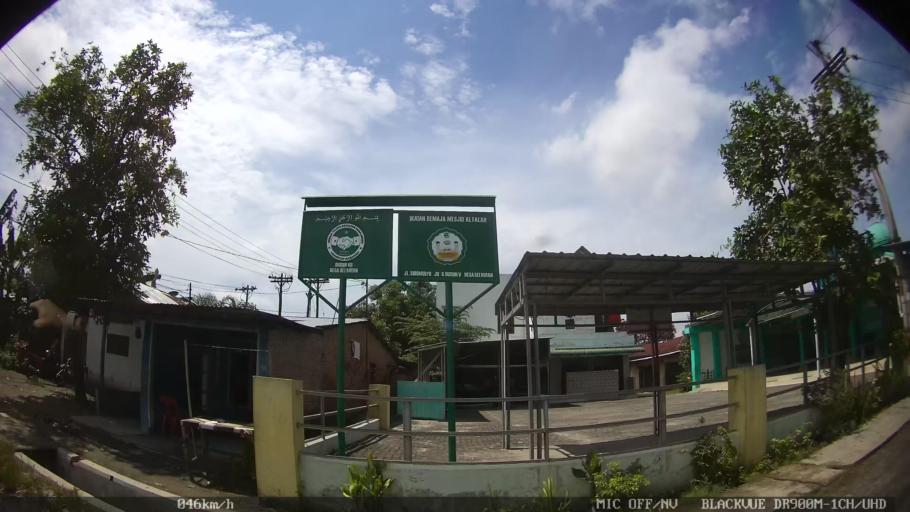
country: ID
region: North Sumatra
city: Percut
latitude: 3.6018
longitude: 98.7872
